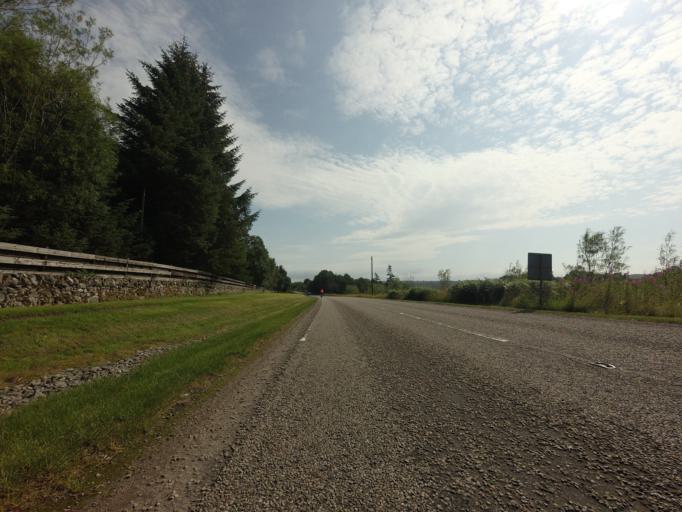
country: GB
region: Scotland
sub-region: Highland
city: Evanton
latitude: 57.9217
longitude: -4.3988
